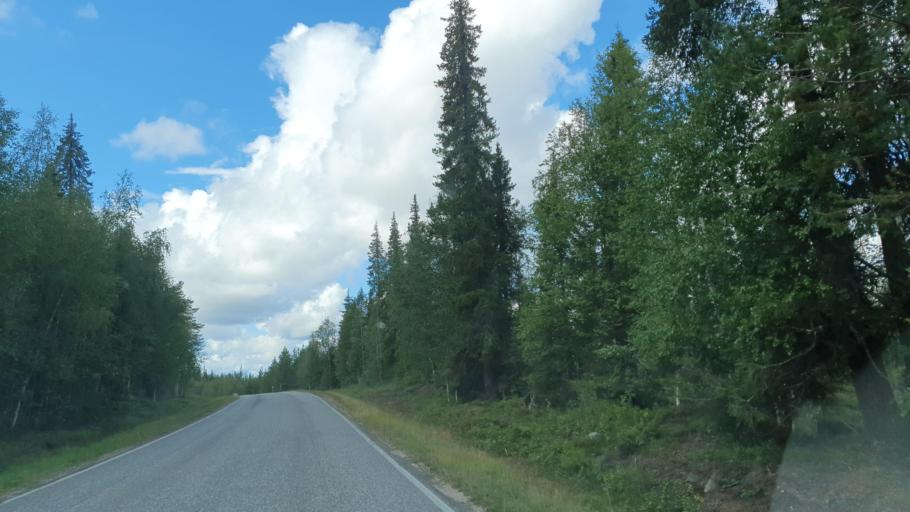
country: FI
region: Lapland
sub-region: Tunturi-Lappi
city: Kolari
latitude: 67.6836
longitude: 24.1248
